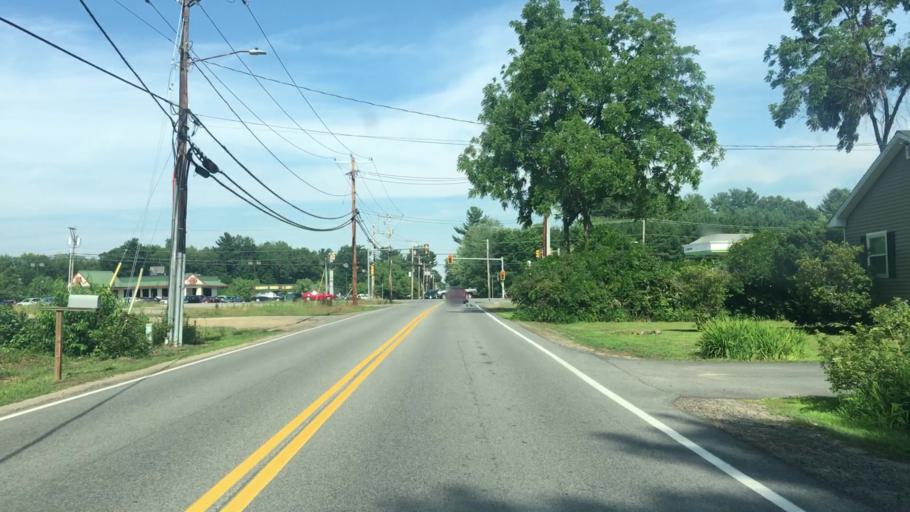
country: US
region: New Hampshire
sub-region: Strafford County
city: Somersworth
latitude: 43.2453
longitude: -70.9008
